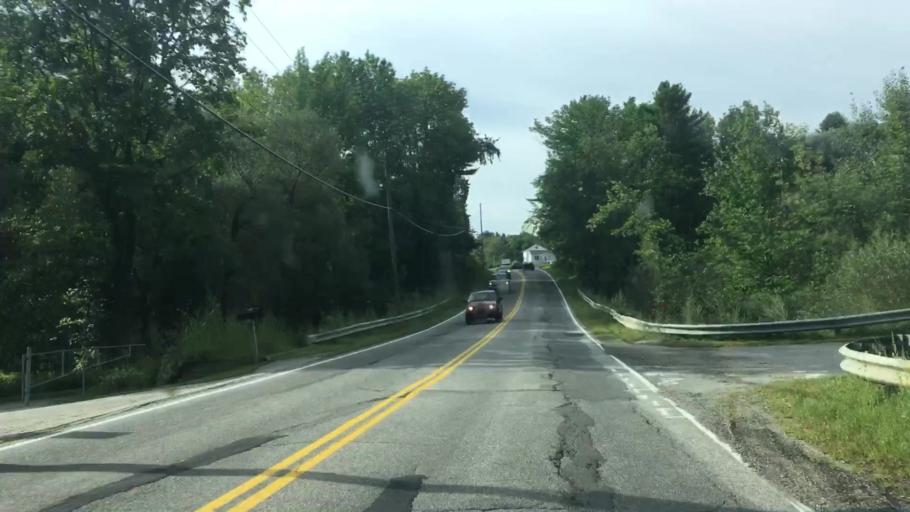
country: US
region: Maine
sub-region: Cumberland County
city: Falmouth
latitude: 43.7427
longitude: -70.2979
